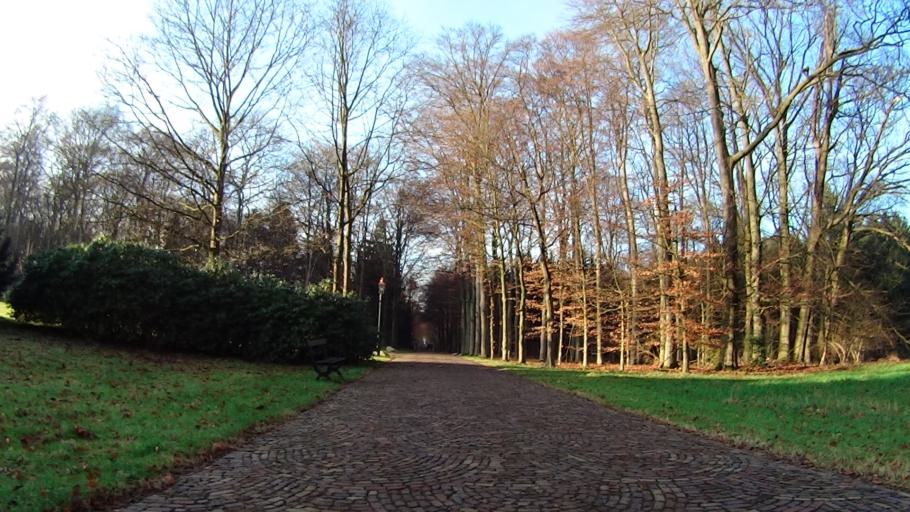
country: NL
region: Utrecht
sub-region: Gemeente Soest
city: Soest
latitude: 52.1388
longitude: 5.2816
